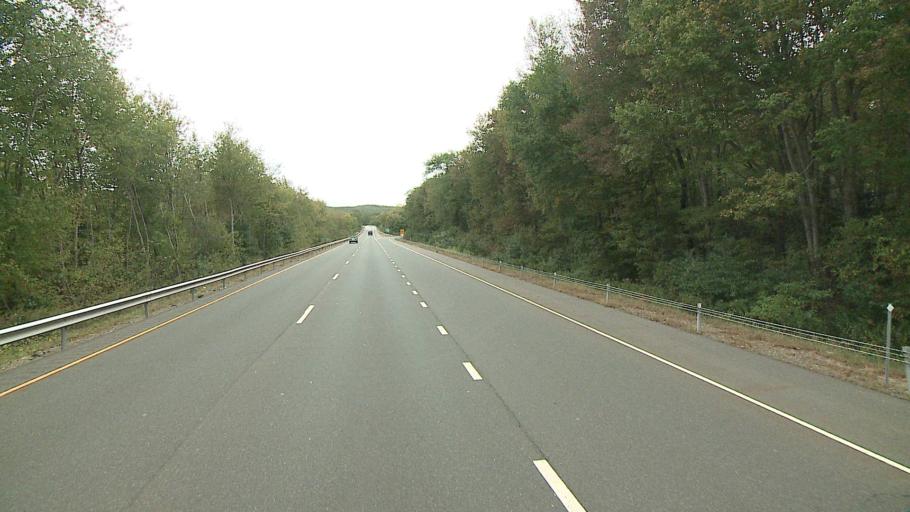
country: US
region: Connecticut
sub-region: Middlesex County
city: Essex Village
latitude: 41.3465
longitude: -72.4004
